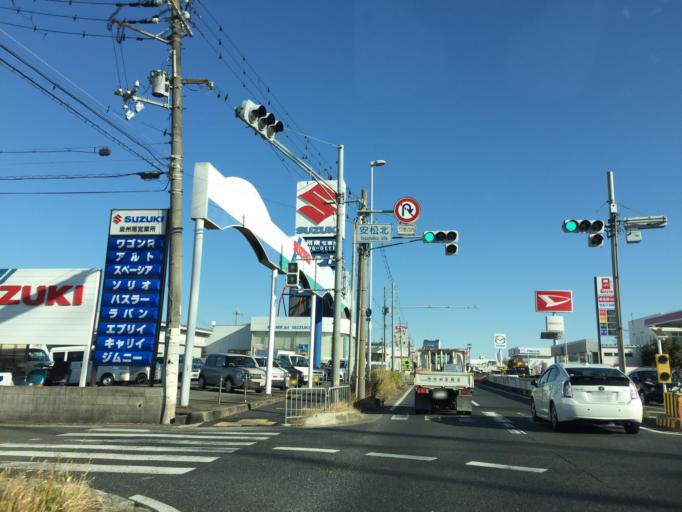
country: JP
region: Osaka
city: Kaizuka
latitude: 34.3948
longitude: 135.3069
